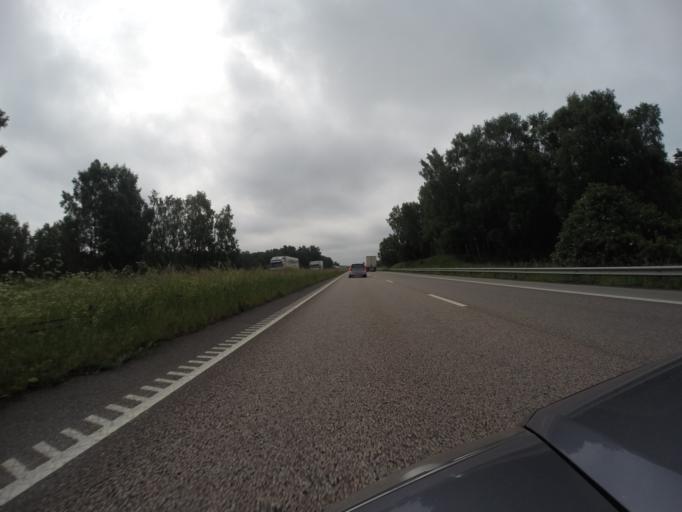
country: SE
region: Skane
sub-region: Kavlinge Kommun
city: Hofterup
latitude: 55.8083
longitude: 12.9506
